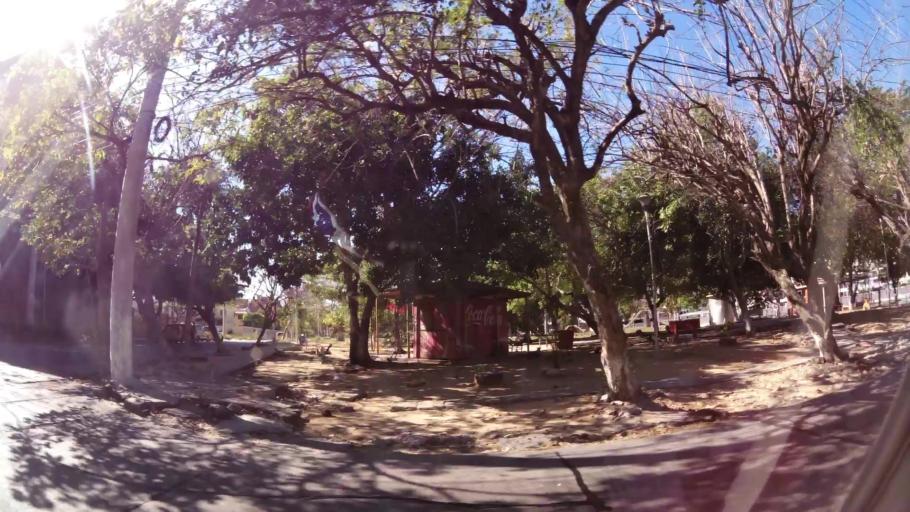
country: CO
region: Atlantico
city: Barranquilla
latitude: 11.0185
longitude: -74.8181
